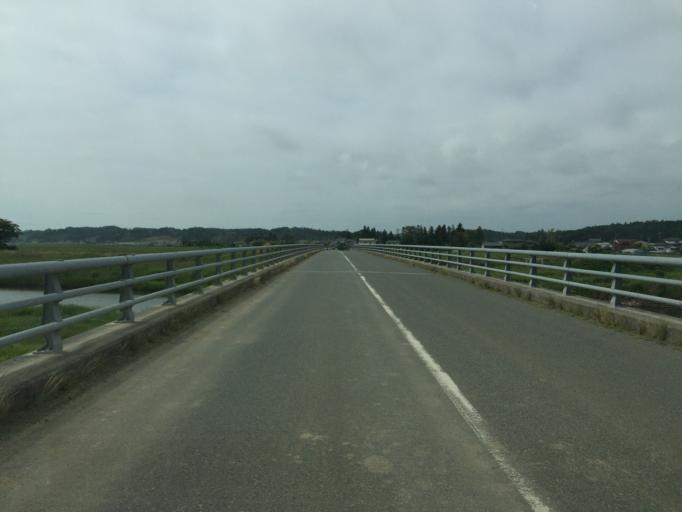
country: JP
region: Fukushima
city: Namie
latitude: 37.6963
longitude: 140.9839
